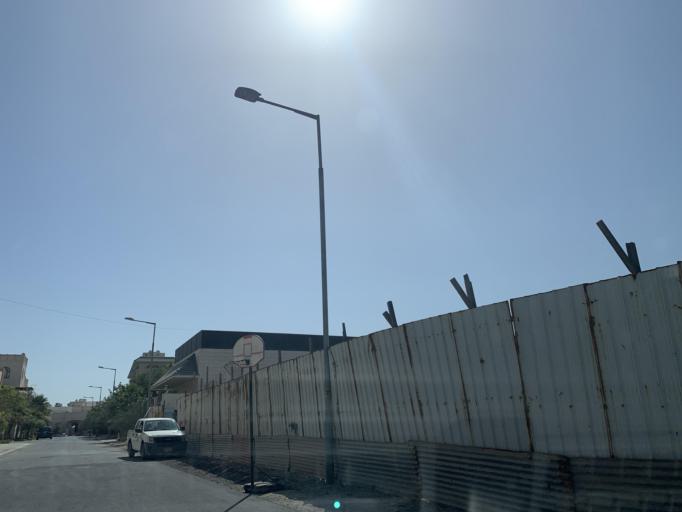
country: BH
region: Manama
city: Manama
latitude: 26.2021
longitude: 50.5737
